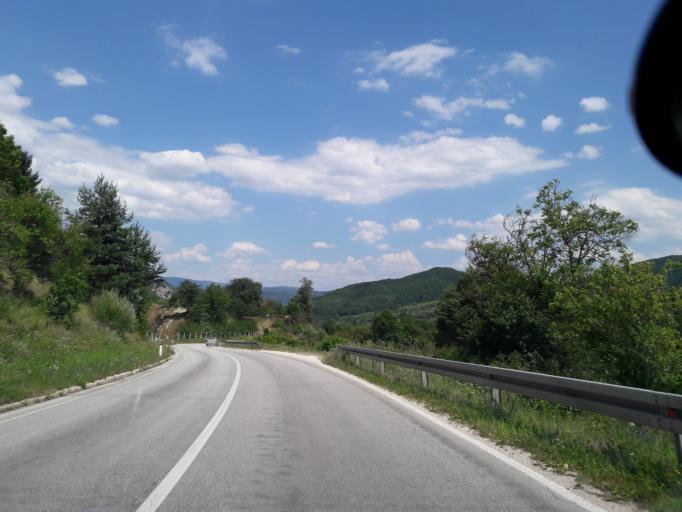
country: BA
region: Republika Srpska
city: Mrkonjic Grad
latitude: 44.4175
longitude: 17.1036
